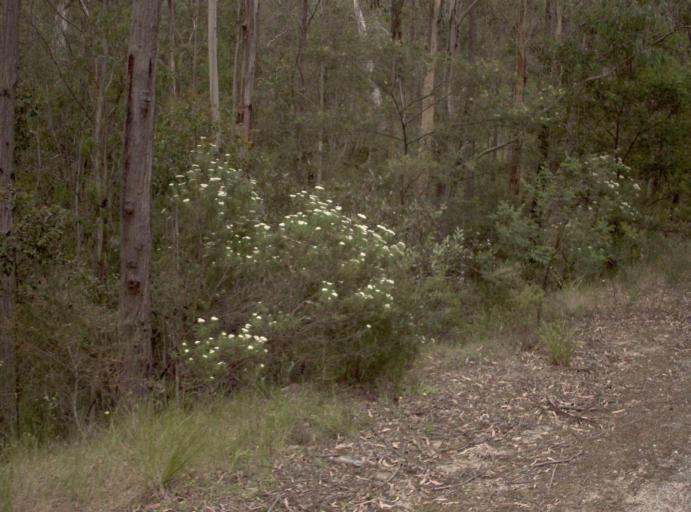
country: AU
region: New South Wales
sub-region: Bombala
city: Bombala
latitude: -37.3508
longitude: 149.2032
